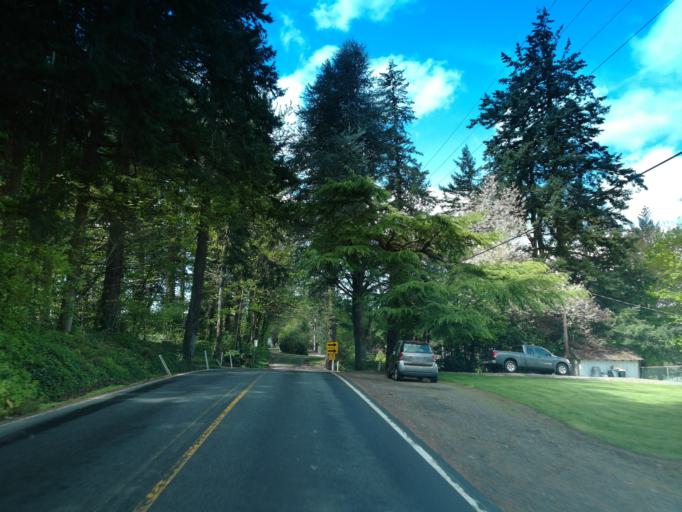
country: US
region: Oregon
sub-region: Clackamas County
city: Damascus
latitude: 45.4325
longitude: -122.4379
